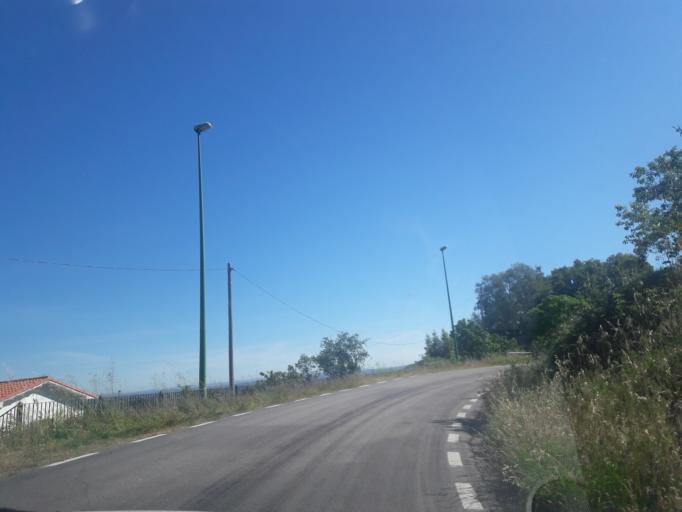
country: ES
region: Castille and Leon
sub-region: Provincia de Salamanca
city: Montemayor del Rio
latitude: 40.3286
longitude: -5.9165
